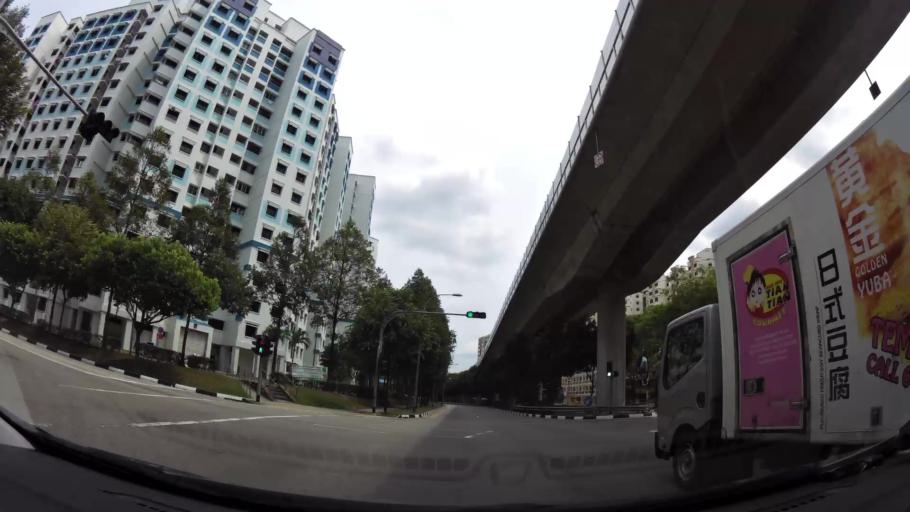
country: MY
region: Johor
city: Johor Bahru
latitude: 1.3377
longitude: 103.7014
